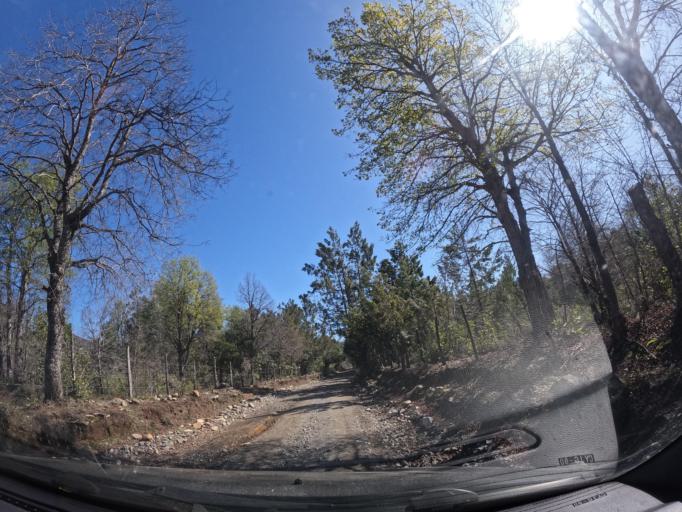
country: CL
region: Maule
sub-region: Provincia de Linares
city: Longavi
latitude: -36.2423
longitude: -71.3496
